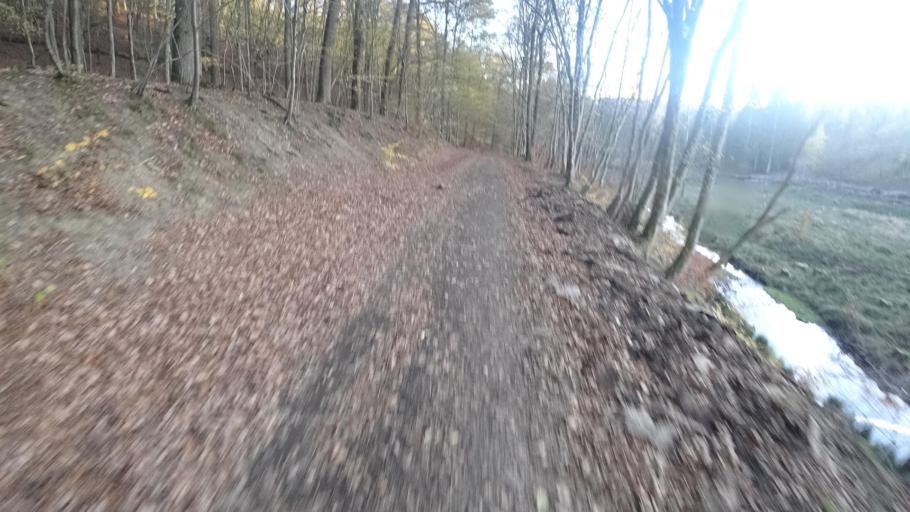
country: DE
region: Rheinland-Pfalz
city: Berg
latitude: 50.5371
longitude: 6.9721
